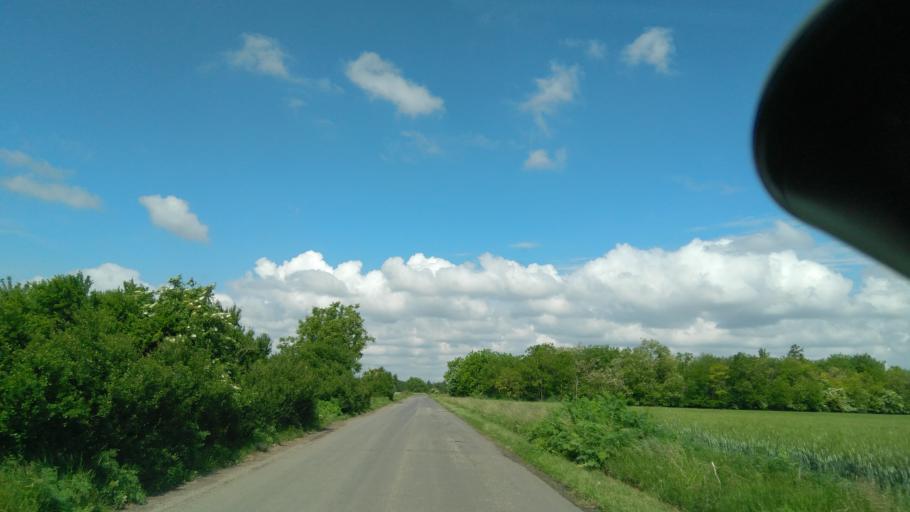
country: HU
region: Bekes
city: Bekes
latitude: 46.8202
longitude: 21.1424
